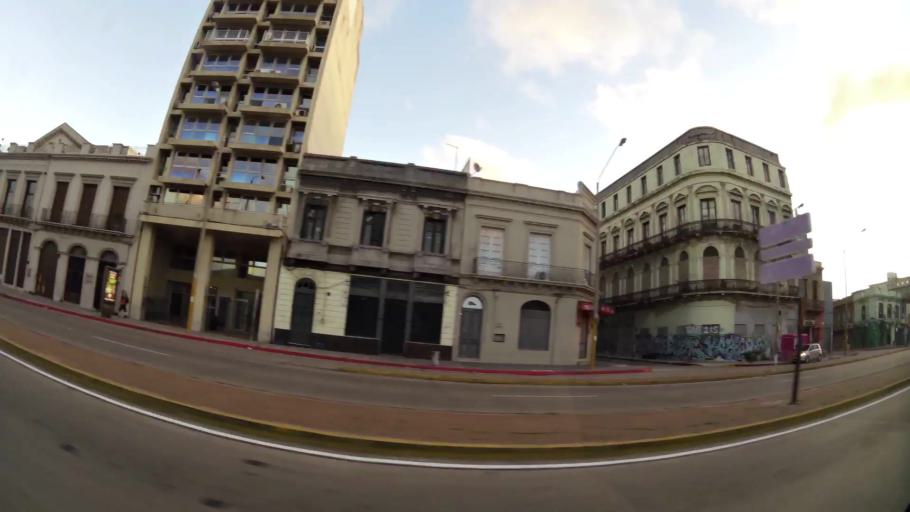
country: UY
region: Montevideo
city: Montevideo
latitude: -34.9047
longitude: -56.2105
